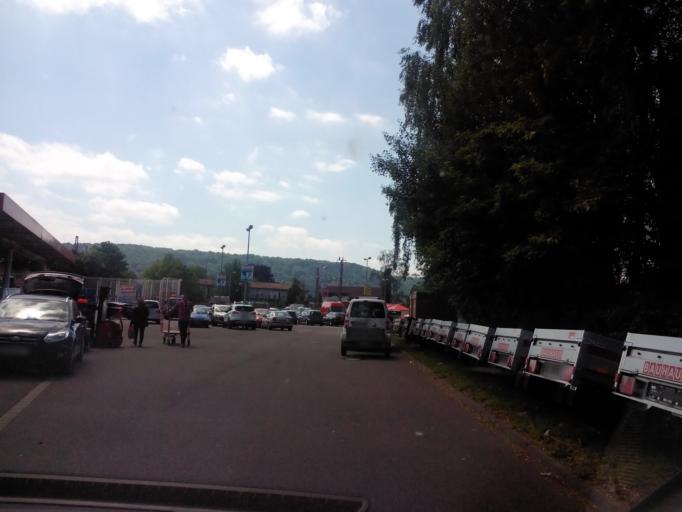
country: DE
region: Saarland
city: Dillingen
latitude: 49.3487
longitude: 6.7298
